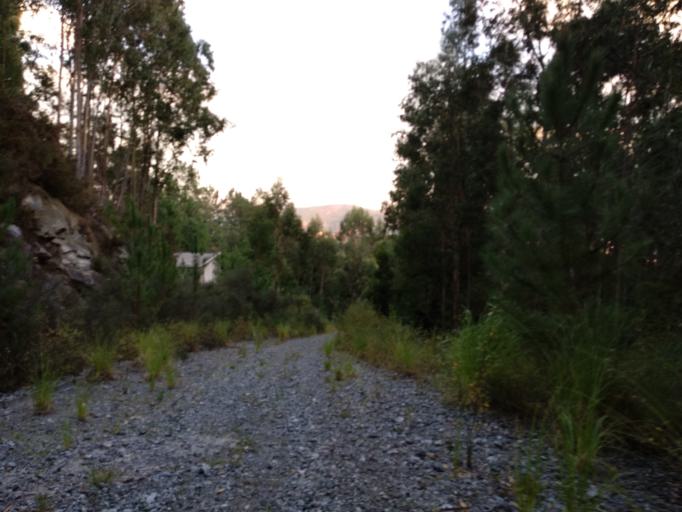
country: ES
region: Galicia
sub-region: Provincia de Pontevedra
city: Moana
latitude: 42.3009
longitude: -8.6941
